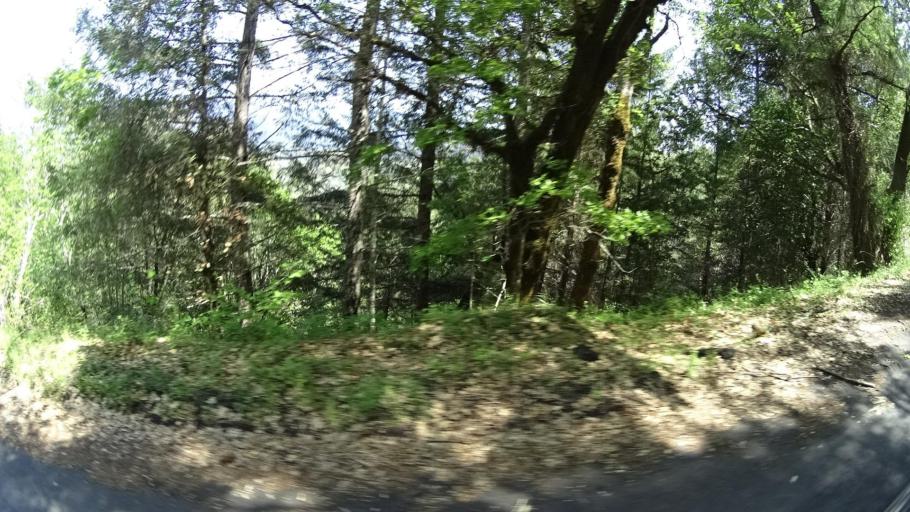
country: US
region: California
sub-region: Humboldt County
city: Redway
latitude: 40.2151
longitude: -123.6577
